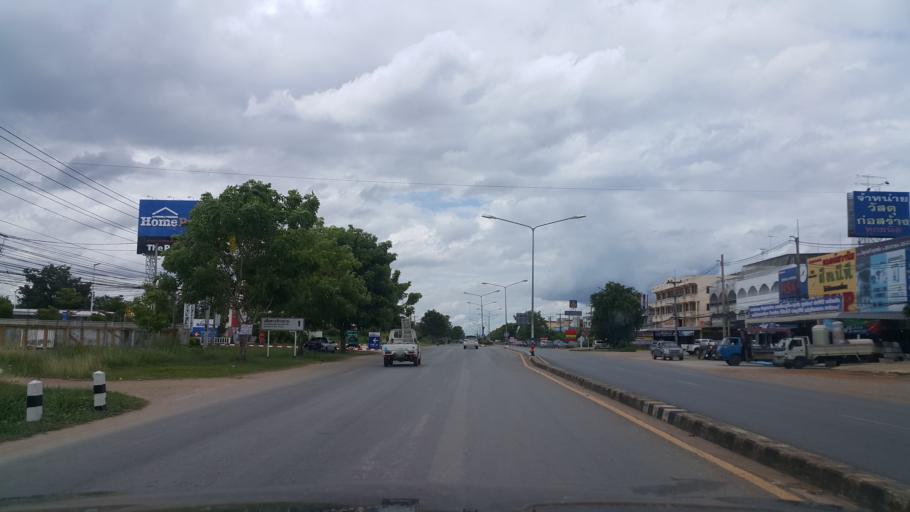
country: TH
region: Sukhothai
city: Sukhothai
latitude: 17.0106
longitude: 99.8061
